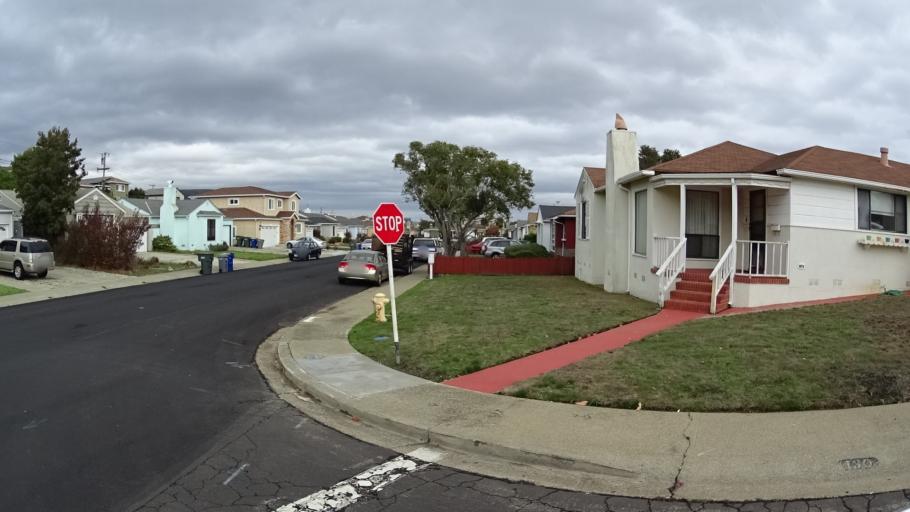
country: US
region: California
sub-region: San Mateo County
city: San Bruno
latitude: 37.6399
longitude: -122.4293
